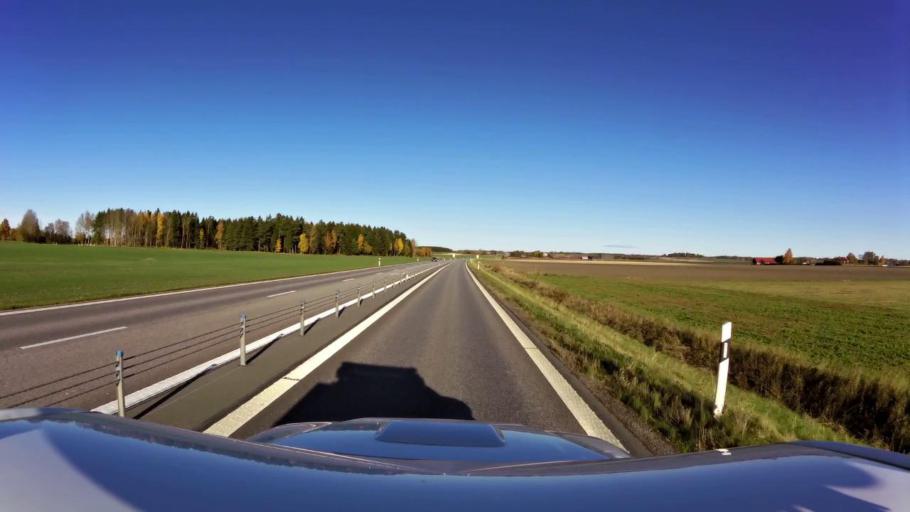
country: SE
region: OEstergoetland
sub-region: Linkopings Kommun
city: Berg
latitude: 58.4560
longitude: 15.5012
